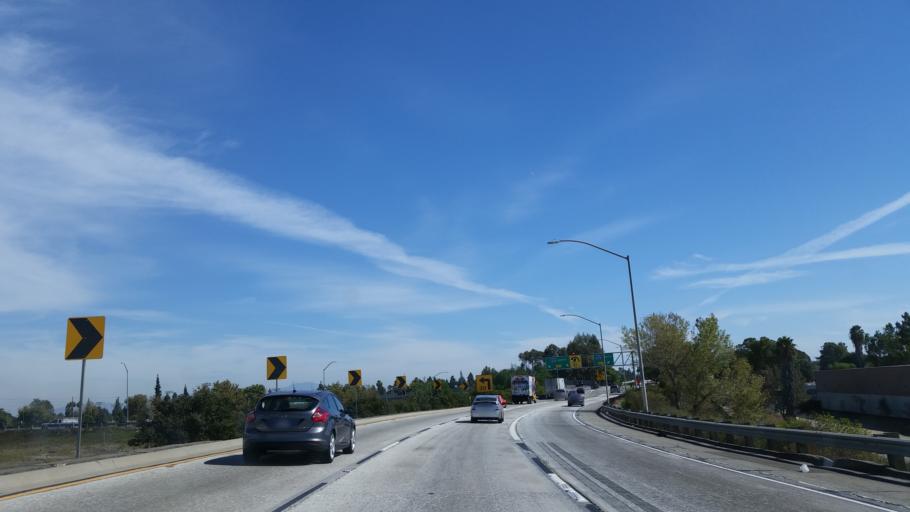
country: US
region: California
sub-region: Los Angeles County
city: Bellflower
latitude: 33.8760
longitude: -118.1057
